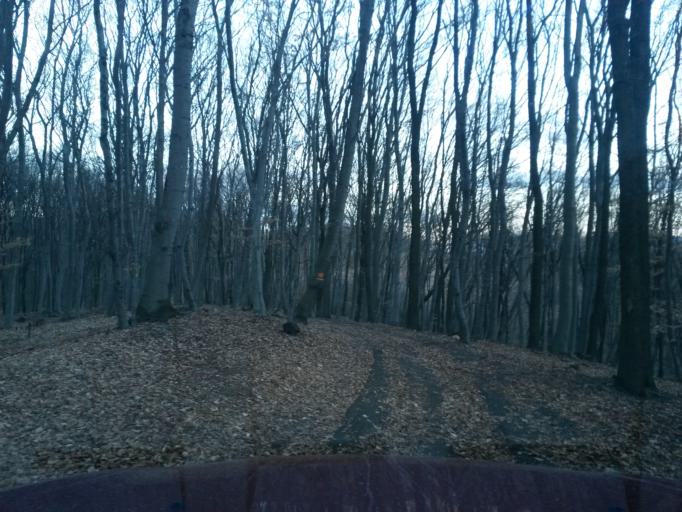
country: SK
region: Kosicky
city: Kosice
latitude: 48.7045
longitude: 21.3725
